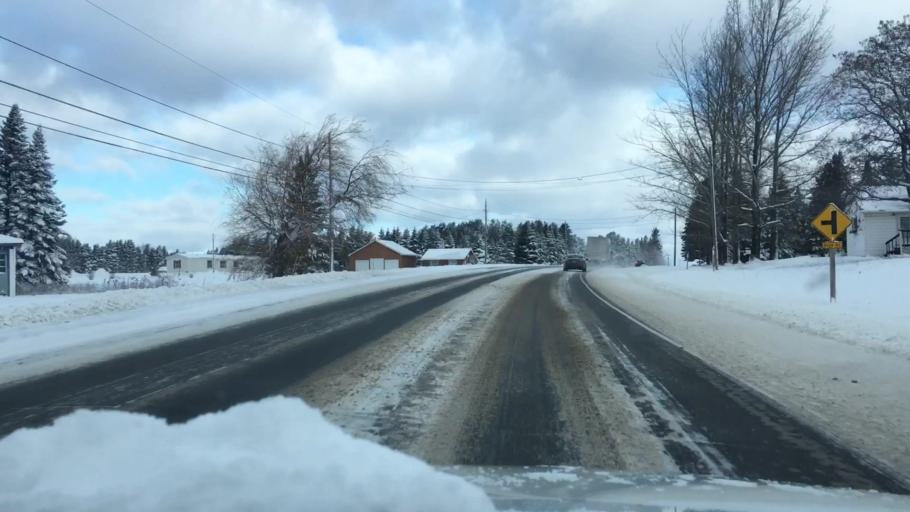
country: US
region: Maine
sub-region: Aroostook County
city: Caribou
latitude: 46.7903
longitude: -67.9908
